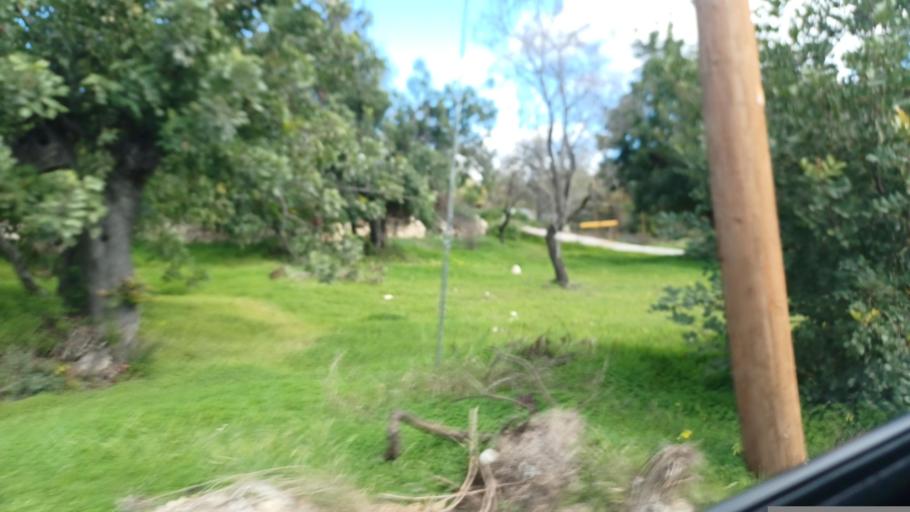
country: CY
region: Limassol
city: Pano Polemidia
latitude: 34.7842
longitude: 32.9785
